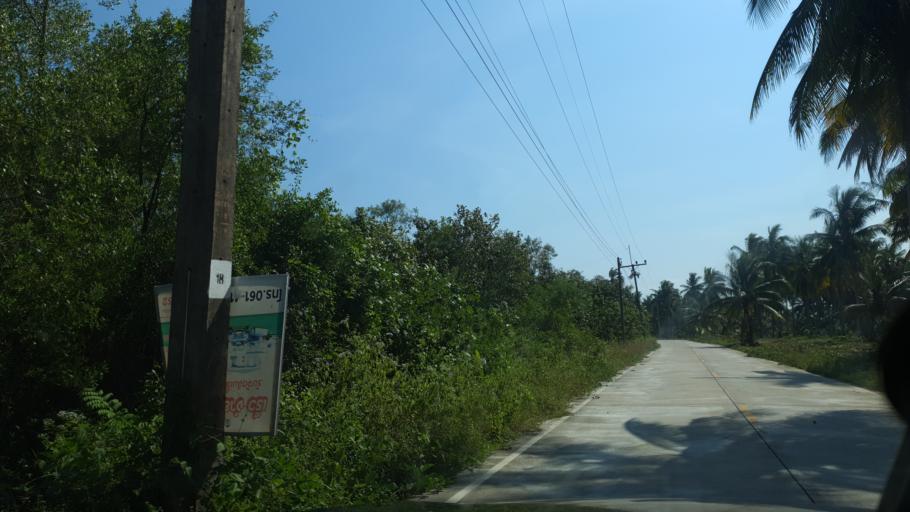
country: TH
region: Surat Thani
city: Tha Chana
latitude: 9.5971
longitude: 99.2054
